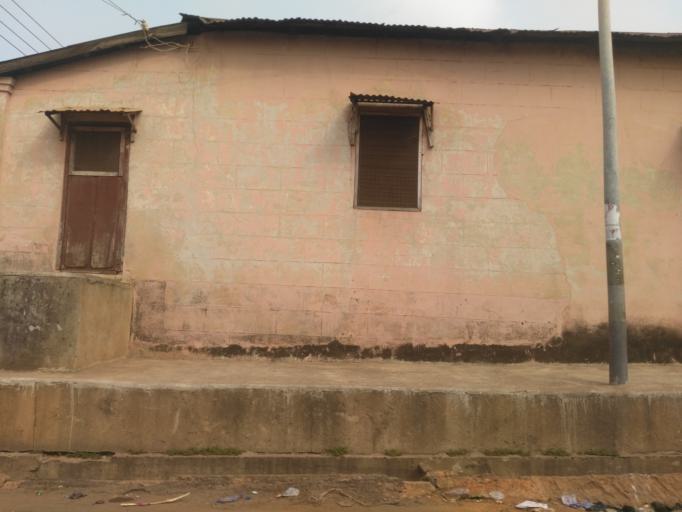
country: GH
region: Ashanti
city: Kumasi
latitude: 6.6908
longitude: -1.6166
